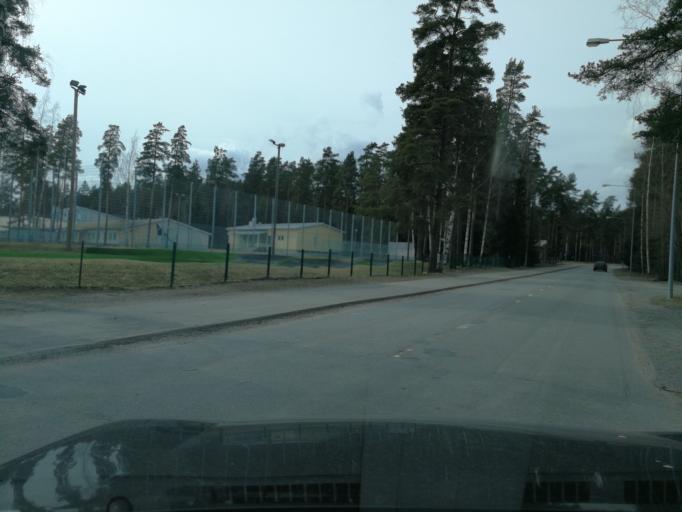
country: FI
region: Uusimaa
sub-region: Helsinki
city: Lohja
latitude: 60.2378
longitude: 24.0708
